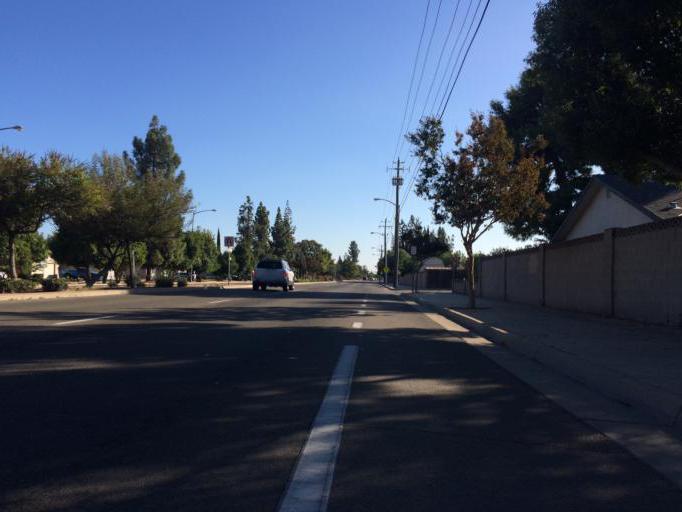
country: US
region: California
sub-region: Fresno County
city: Clovis
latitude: 36.8126
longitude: -119.6821
